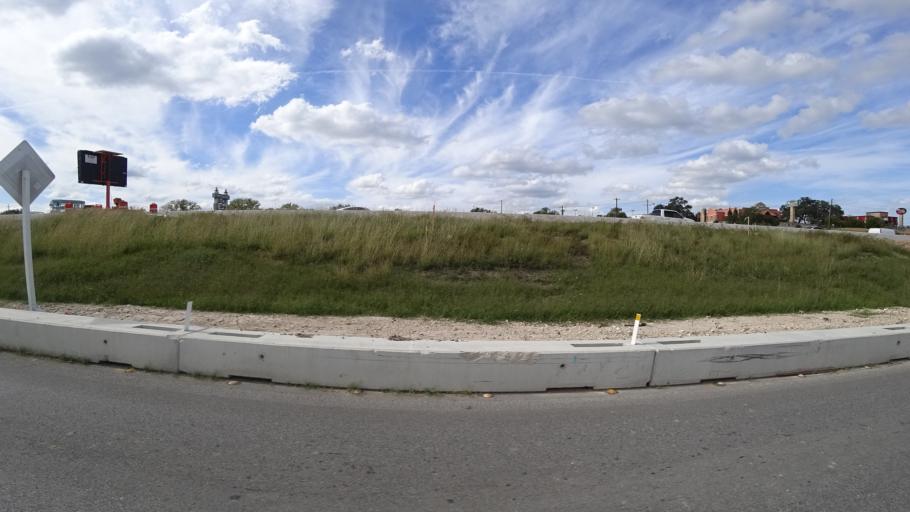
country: US
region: Texas
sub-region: Travis County
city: Onion Creek
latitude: 30.1964
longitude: -97.7652
